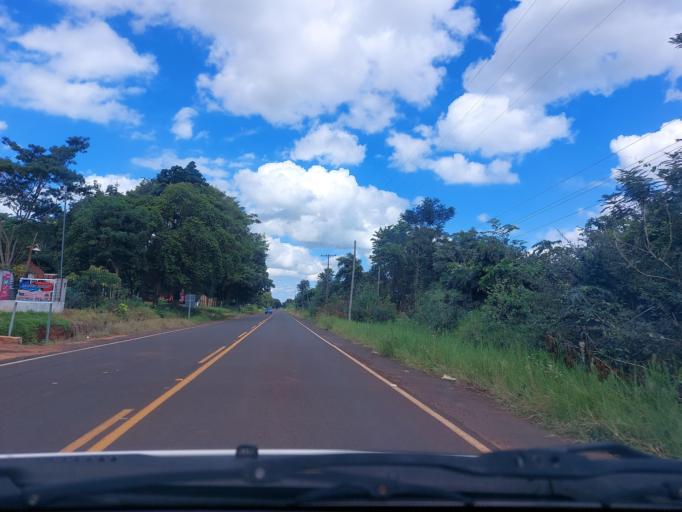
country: PY
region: San Pedro
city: Guayaybi
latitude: -24.5884
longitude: -56.5196
